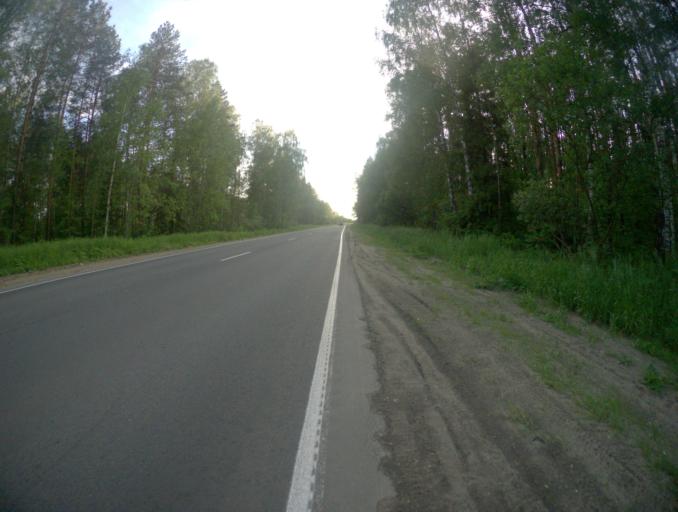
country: RU
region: Vladimir
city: Gus'-Khrustal'nyy
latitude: 55.6357
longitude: 40.7646
